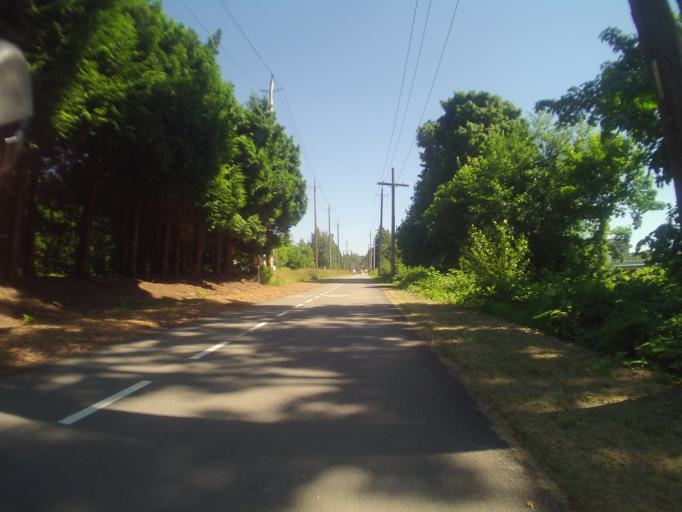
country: CA
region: British Columbia
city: Vancouver
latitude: 49.2491
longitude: -123.1513
